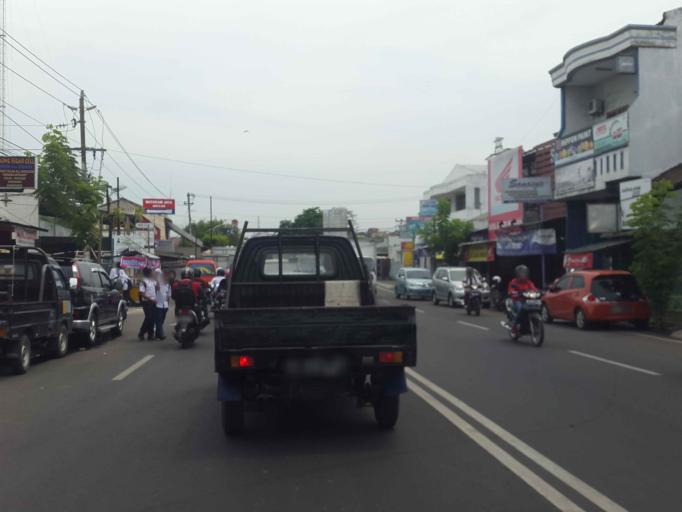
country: ID
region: Central Java
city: Semarang
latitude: -7.0103
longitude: 110.4404
